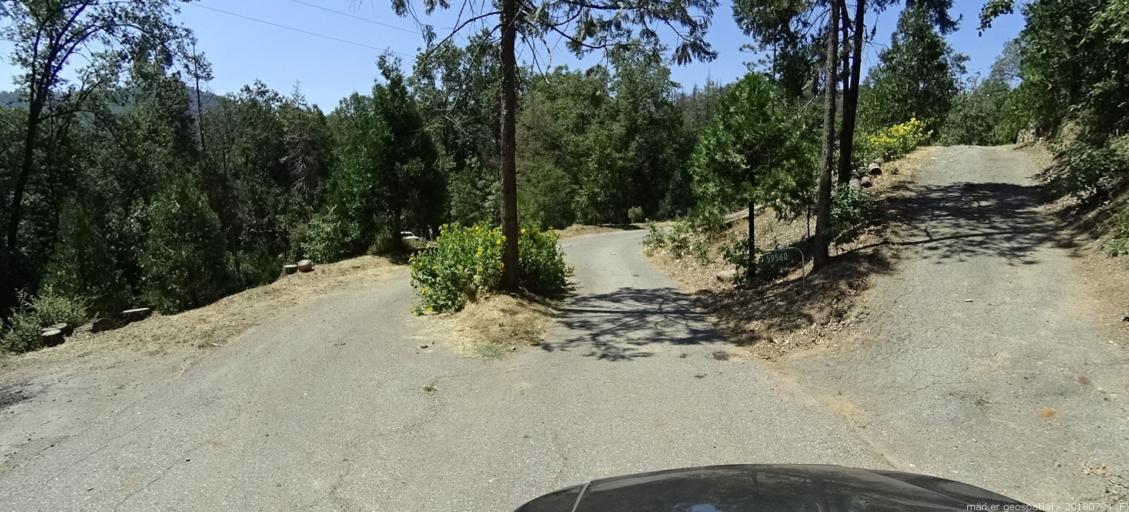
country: US
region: California
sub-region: Fresno County
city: Auberry
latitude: 37.2313
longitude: -119.4627
